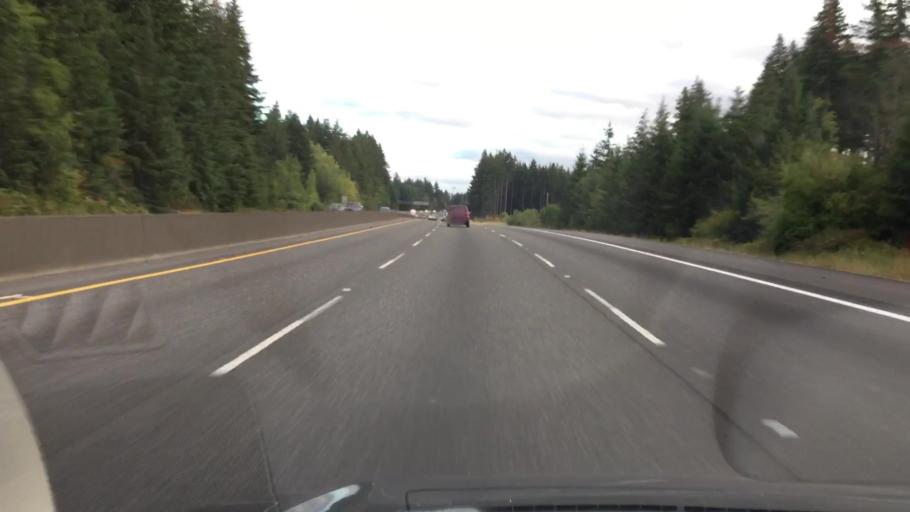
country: US
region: Washington
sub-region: Cowlitz County
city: Castle Rock
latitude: 46.3634
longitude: -122.9079
